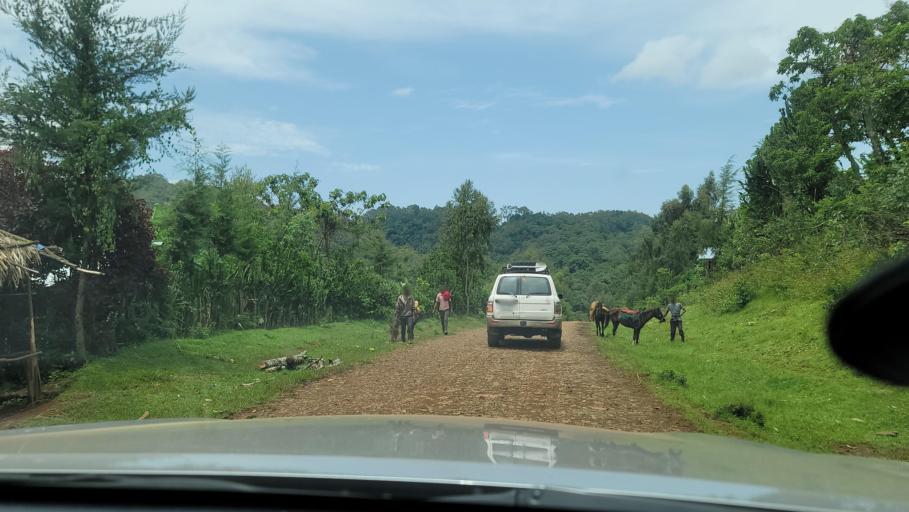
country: ET
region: Southern Nations, Nationalities, and People's Region
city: Bonga
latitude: 7.6915
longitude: 36.2443
